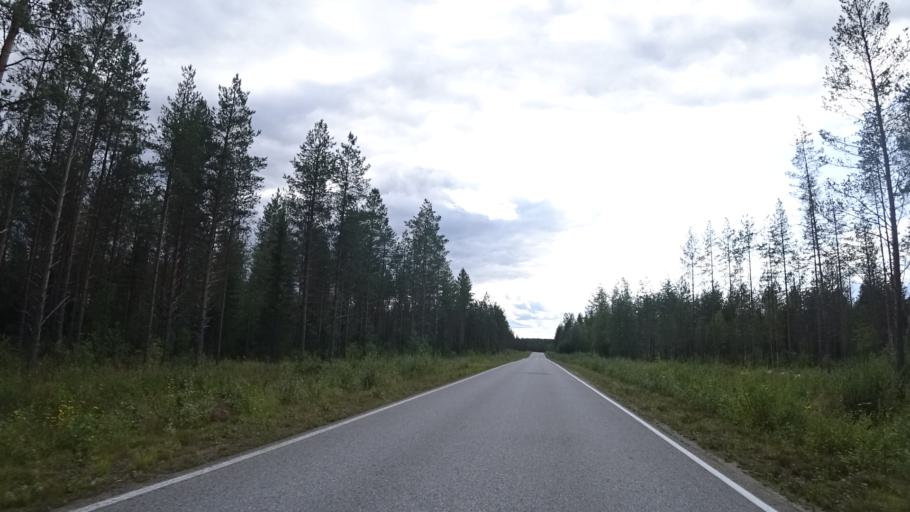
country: FI
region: North Karelia
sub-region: Joensuu
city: Ilomantsi
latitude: 62.4293
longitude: 31.0472
